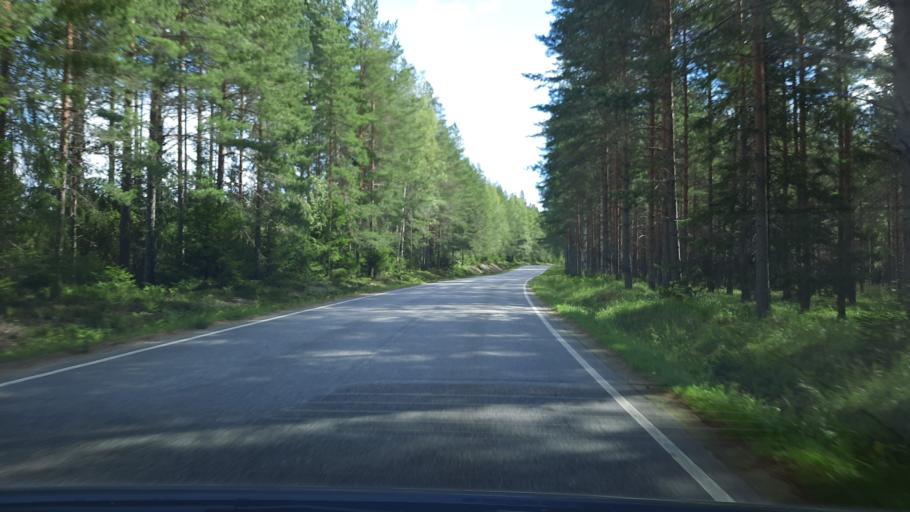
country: FI
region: Pirkanmaa
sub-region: Etelae-Pirkanmaa
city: Urjala
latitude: 61.1719
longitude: 23.3857
